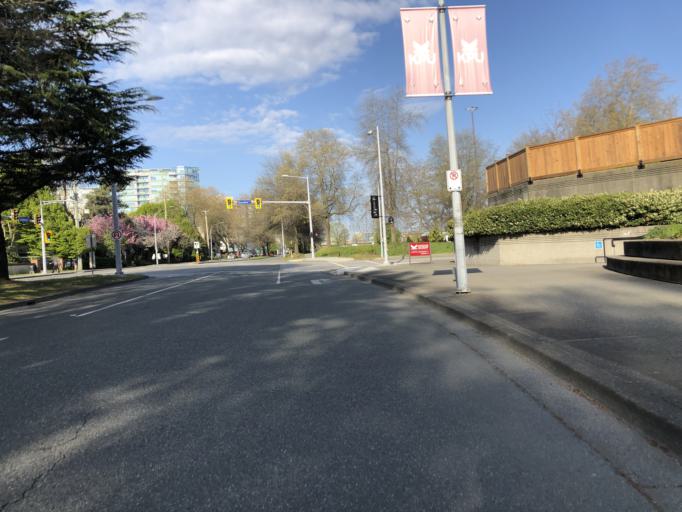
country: CA
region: British Columbia
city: Richmond
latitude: 49.1739
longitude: -123.1277
